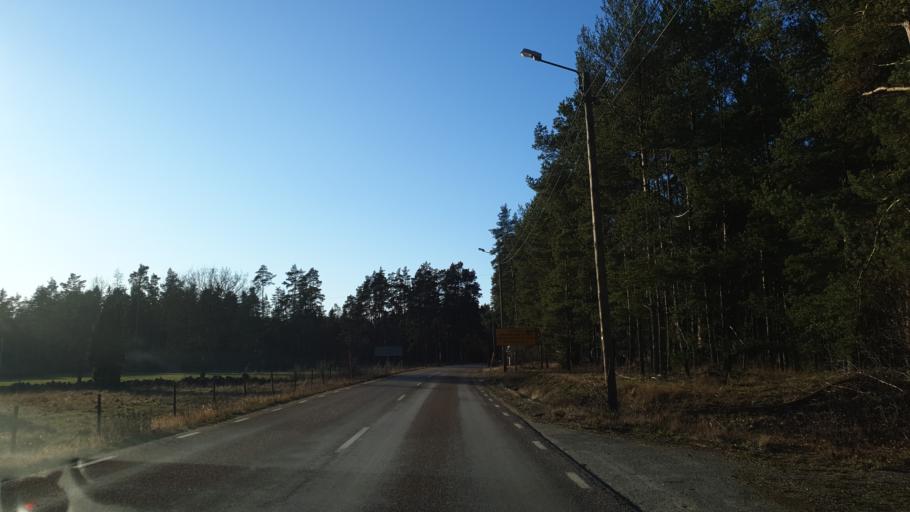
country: SE
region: Blekinge
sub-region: Karlskrona Kommun
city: Nattraby
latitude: 56.2184
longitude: 15.4003
